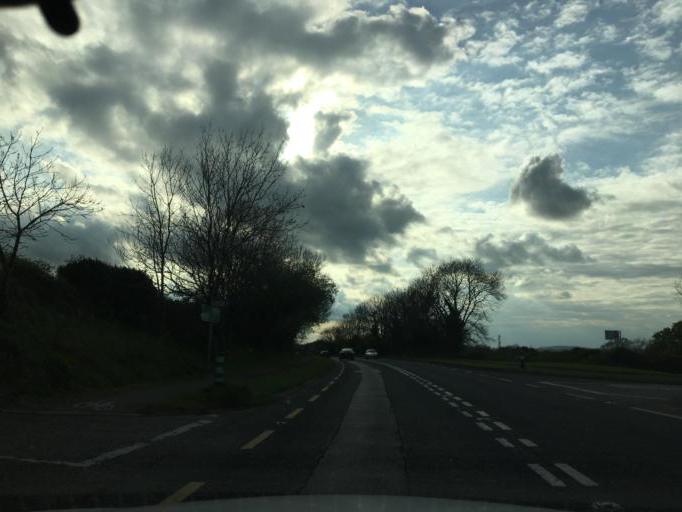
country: IE
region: Leinster
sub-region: Loch Garman
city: Loch Garman
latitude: 52.3392
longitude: -6.5302
